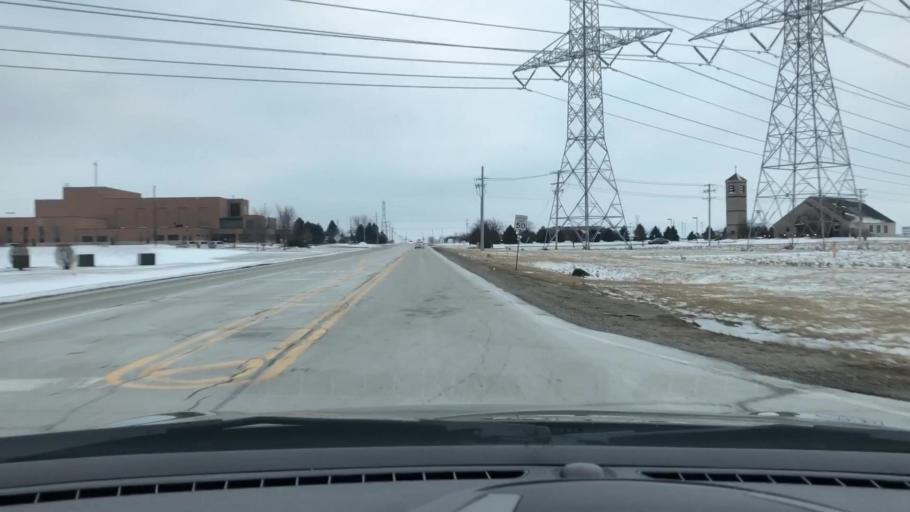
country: US
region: Illinois
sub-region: Will County
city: New Lenox
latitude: 41.4969
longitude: -88.0039
